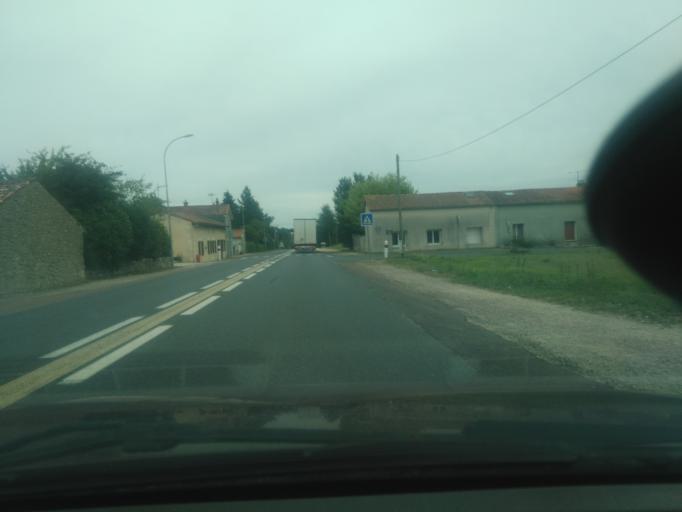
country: FR
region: Poitou-Charentes
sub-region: Departement de la Vienne
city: Sevres-Anxaumont
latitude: 46.5603
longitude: 0.4457
